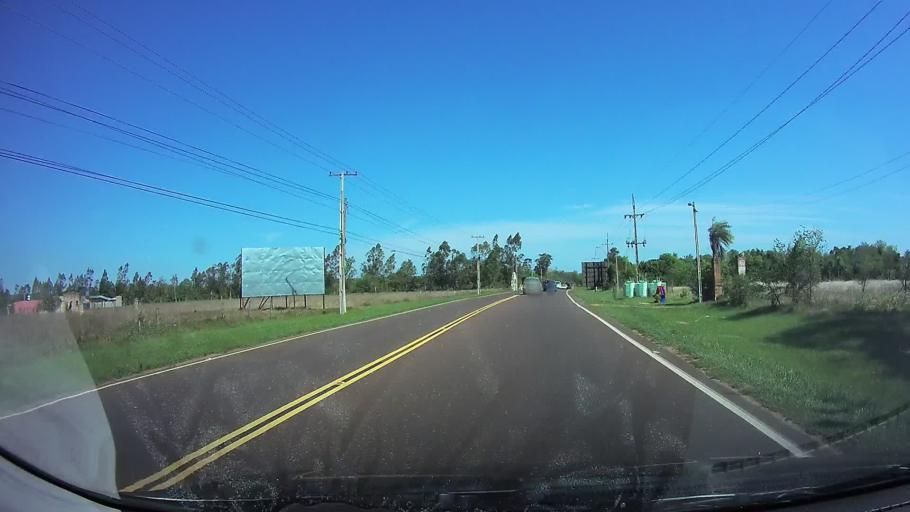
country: PY
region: Central
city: Ypacarai
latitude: -25.3640
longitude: -57.2646
